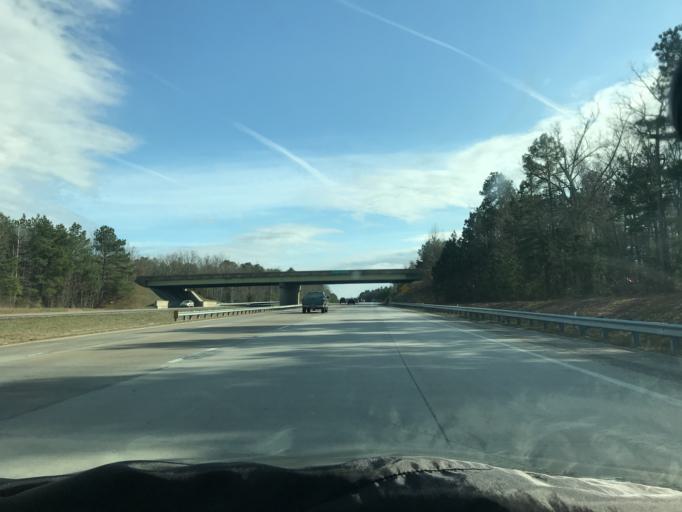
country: US
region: Virginia
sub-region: Chesterfield County
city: Brandermill
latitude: 37.4518
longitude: -77.6376
